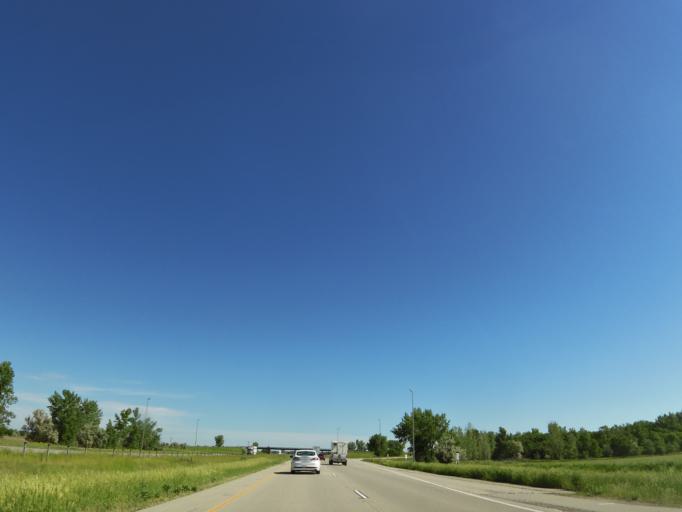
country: US
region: Minnesota
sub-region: Clay County
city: Glyndon
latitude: 46.7502
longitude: -96.5216
